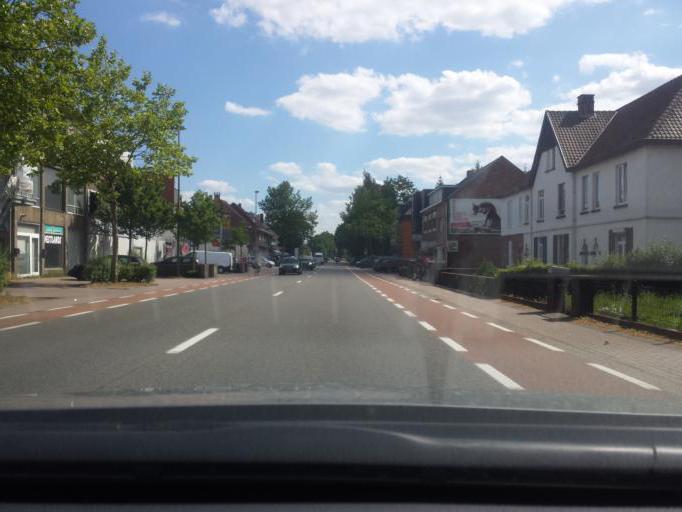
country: BE
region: Flanders
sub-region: Provincie Limburg
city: Beringen
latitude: 51.0743
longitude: 5.2200
